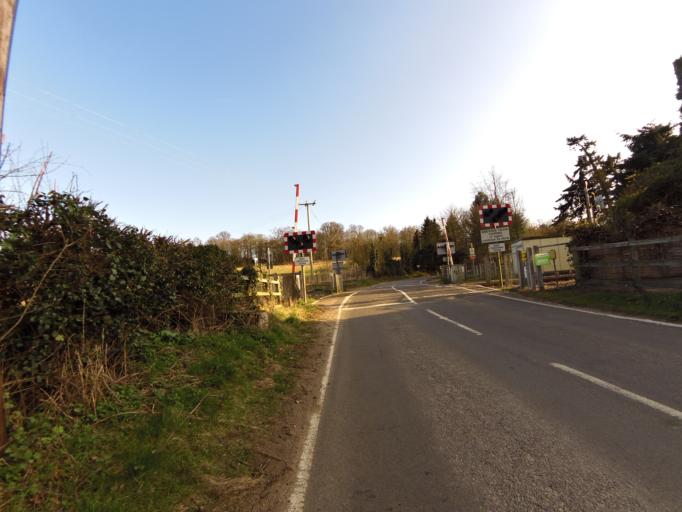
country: GB
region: England
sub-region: Suffolk
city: Kesgrave
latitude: 52.0800
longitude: 1.2543
